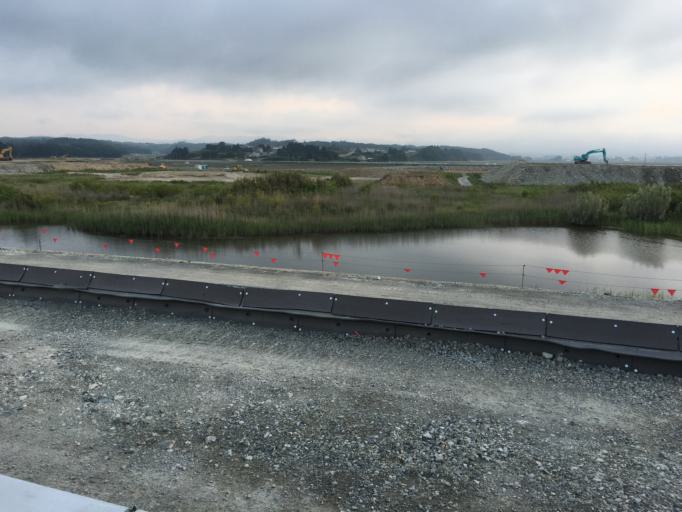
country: JP
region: Miyagi
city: Marumori
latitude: 37.7720
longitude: 140.9888
